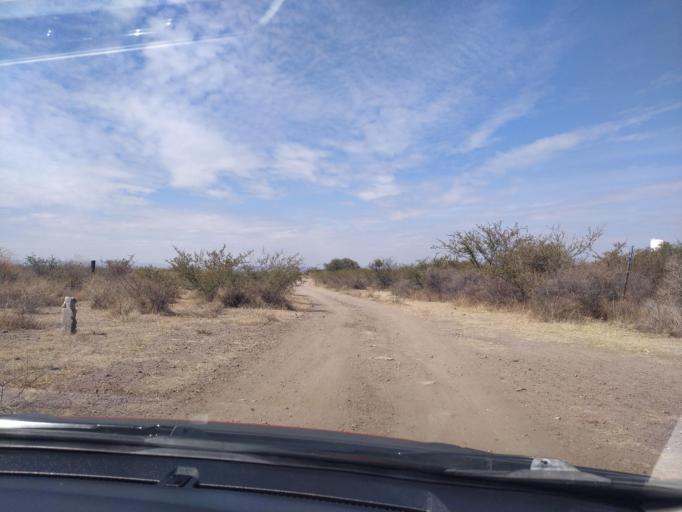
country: MX
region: Guanajuato
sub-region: San Francisco del Rincon
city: San Ignacio de Hidalgo
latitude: 20.8815
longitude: -101.8444
